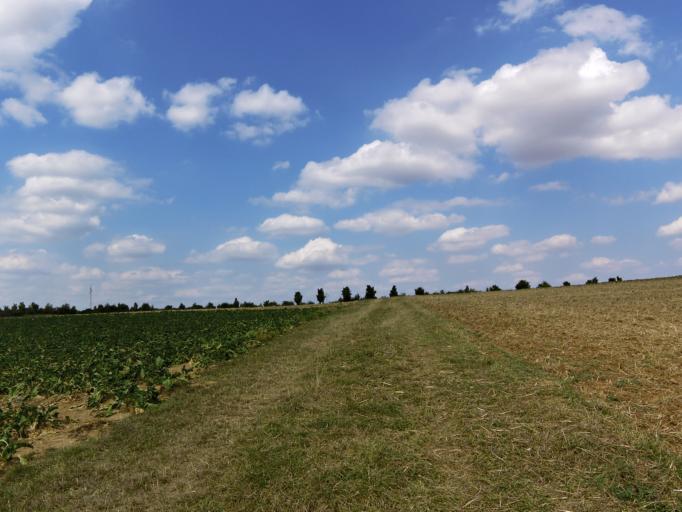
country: DE
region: Bavaria
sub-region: Regierungsbezirk Unterfranken
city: Estenfeld
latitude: 49.8374
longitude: 10.0027
